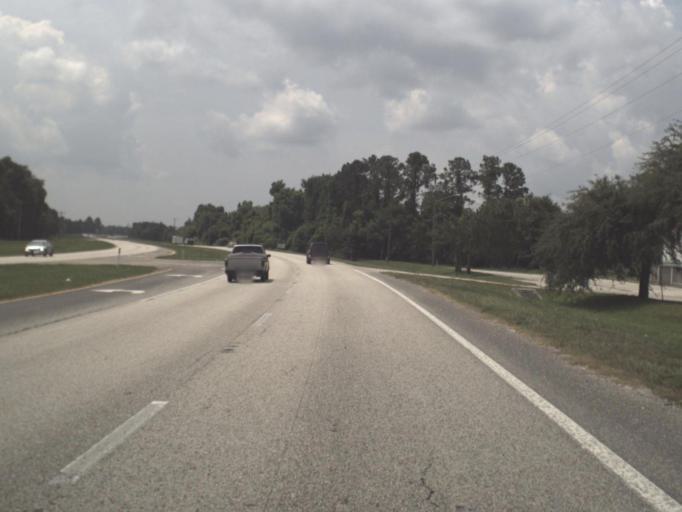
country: US
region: Florida
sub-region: Clay County
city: Green Cove Springs
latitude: 29.9709
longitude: -81.6763
